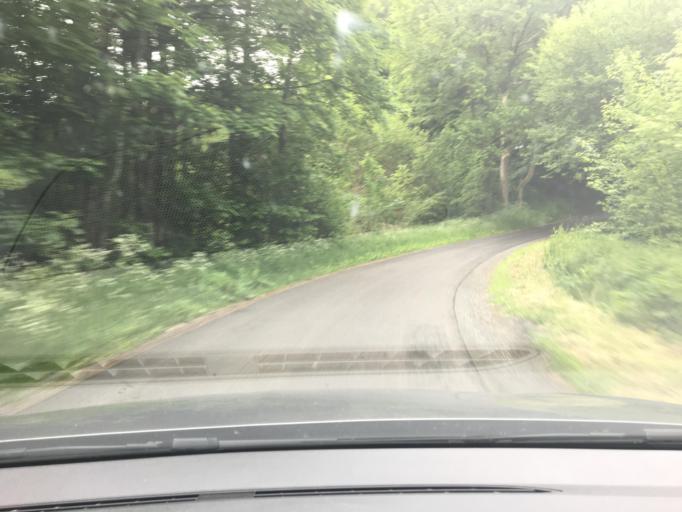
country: DK
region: South Denmark
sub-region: Fredericia Kommune
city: Taulov
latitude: 55.5537
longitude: 9.5363
